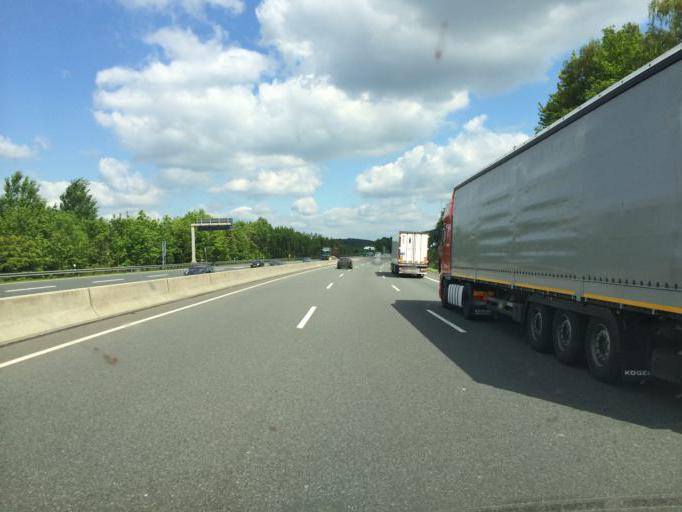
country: DE
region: Lower Saxony
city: Buchholz
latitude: 52.2205
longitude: 9.1256
